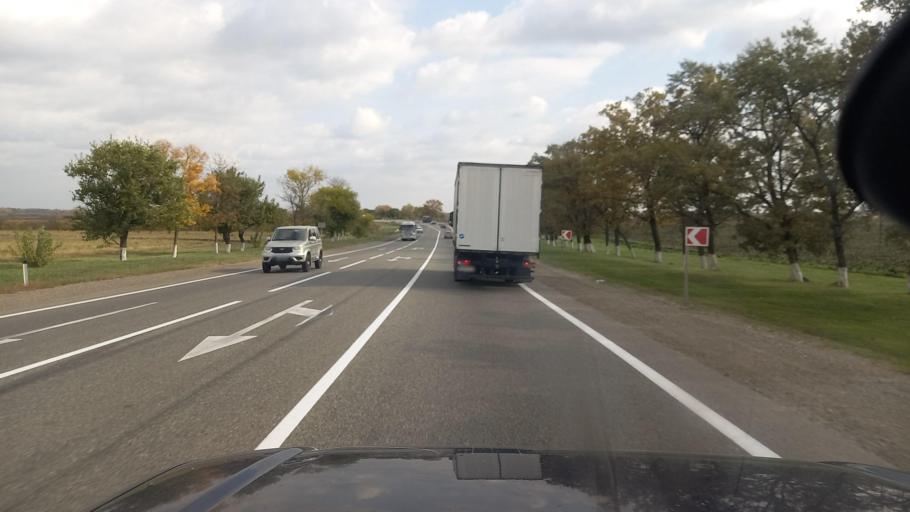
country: RU
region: Krasnodarskiy
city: Kholmskiy
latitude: 44.8478
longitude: 38.4266
